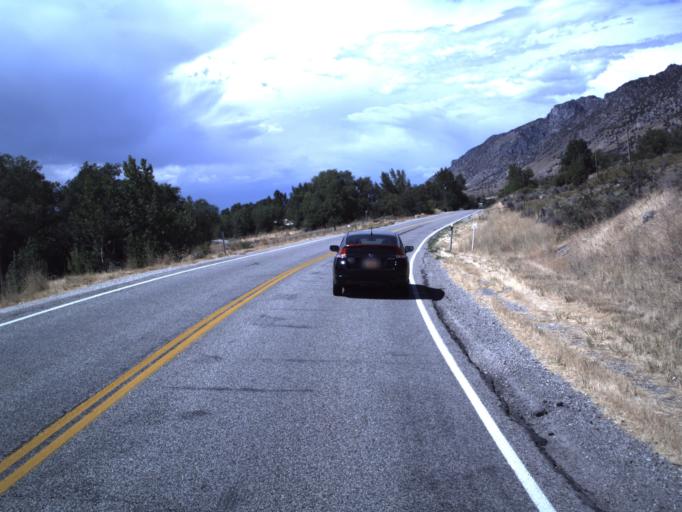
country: US
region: Utah
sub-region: Box Elder County
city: Brigham City
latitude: 41.5587
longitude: -112.0223
